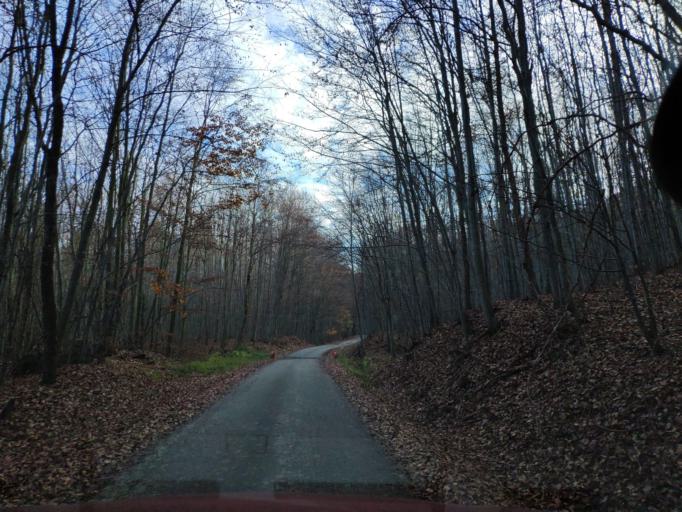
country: HU
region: Borsod-Abauj-Zemplen
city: Gonc
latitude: 48.5957
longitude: 21.4500
